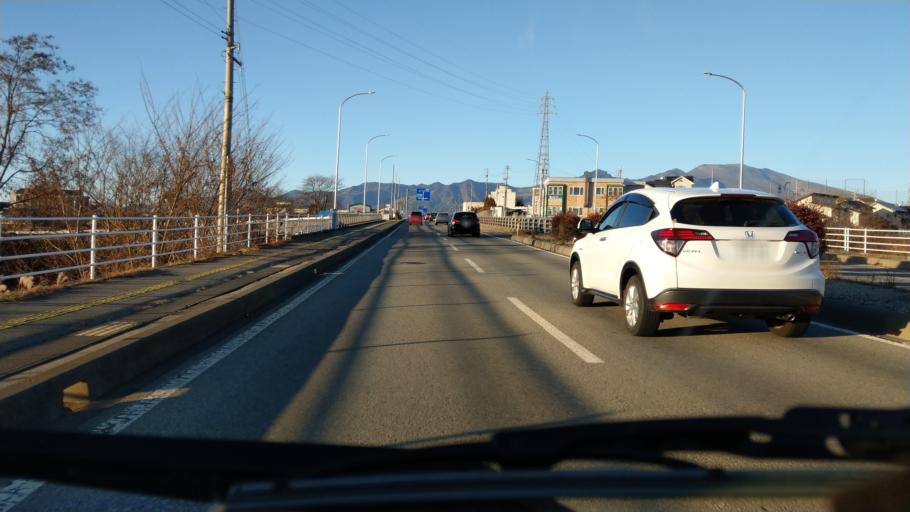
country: JP
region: Nagano
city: Saku
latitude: 36.2622
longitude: 138.4673
